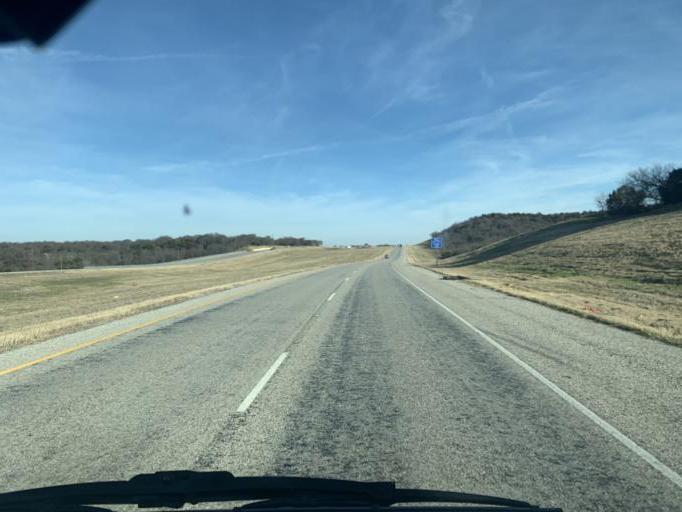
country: US
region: Texas
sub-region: Dallas County
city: Cedar Hill
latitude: 32.6243
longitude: -96.9758
